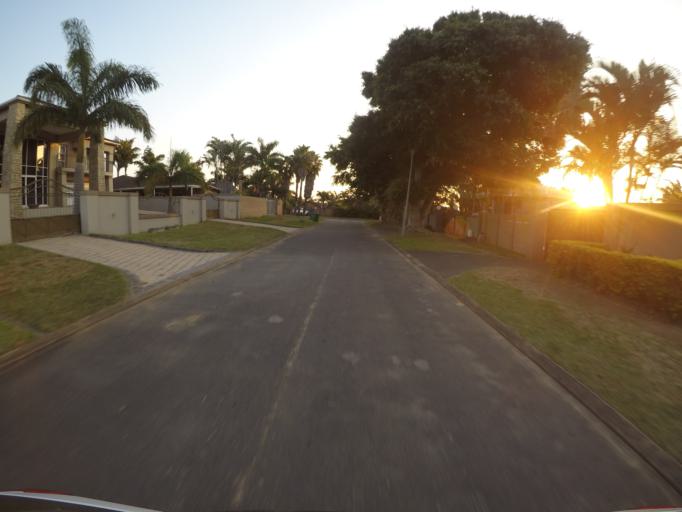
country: ZA
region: KwaZulu-Natal
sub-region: uThungulu District Municipality
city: Richards Bay
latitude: -28.7646
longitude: 32.1210
